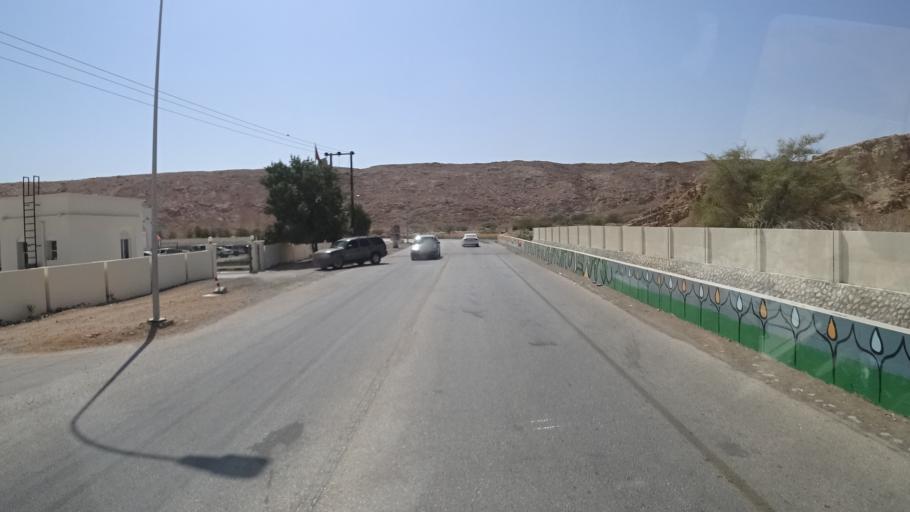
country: OM
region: Ash Sharqiyah
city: Sur
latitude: 22.5628
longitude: 59.5446
